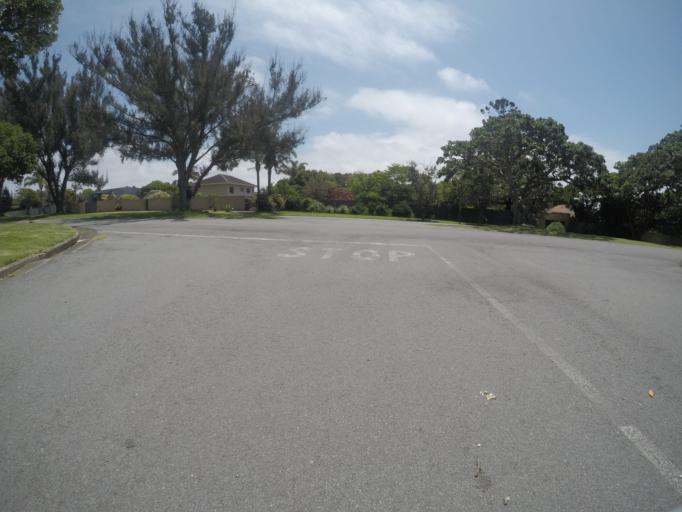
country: ZA
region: Eastern Cape
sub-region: Buffalo City Metropolitan Municipality
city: East London
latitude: -32.9973
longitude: 27.9300
